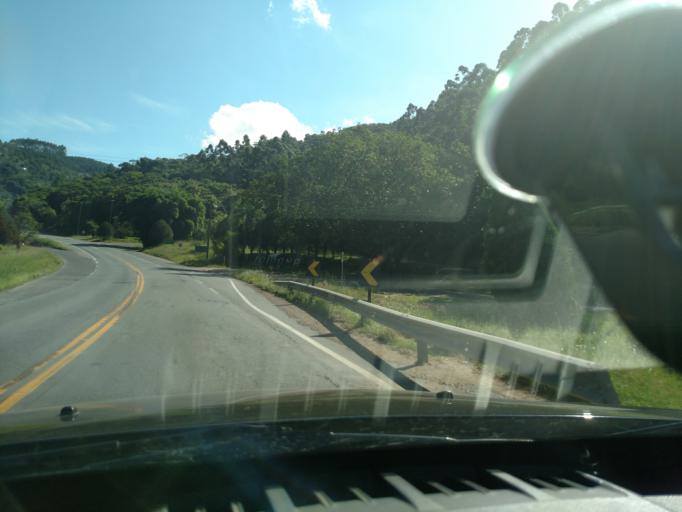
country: BR
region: Santa Catarina
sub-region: Ibirama
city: Ibirama
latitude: -27.0784
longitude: -49.4984
